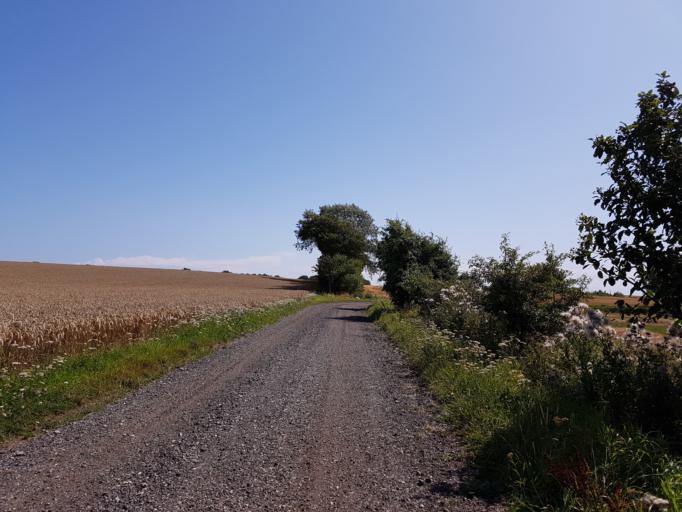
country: DK
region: Zealand
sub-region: Guldborgsund Kommune
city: Nykobing Falster
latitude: 54.5732
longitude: 11.9536
